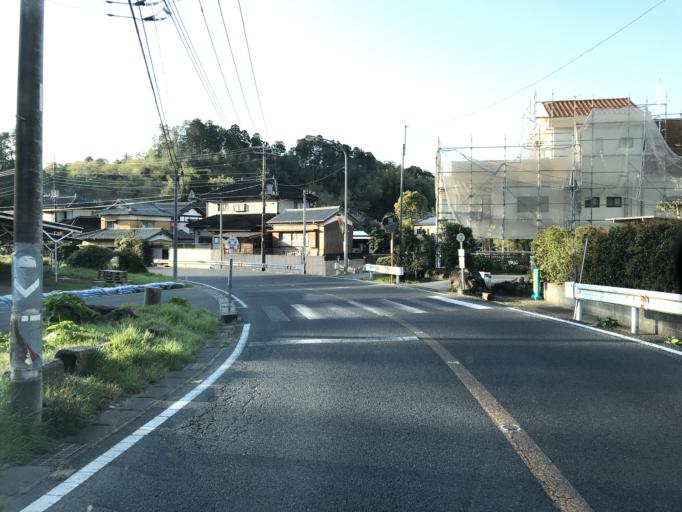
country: JP
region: Chiba
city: Yokaichiba
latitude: 35.7330
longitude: 140.5570
